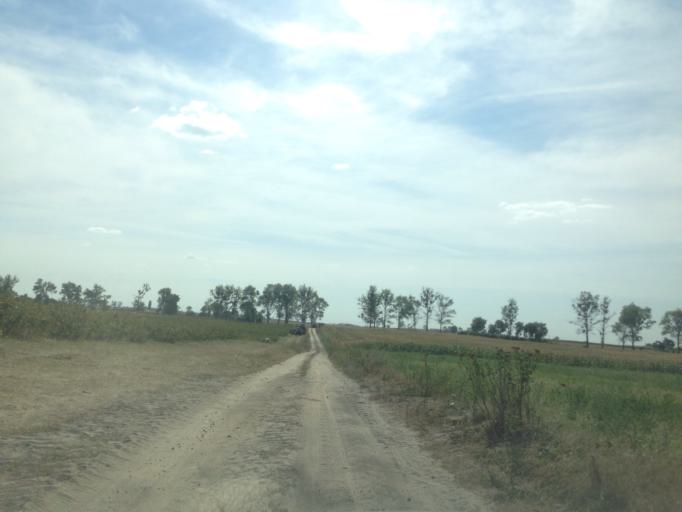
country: PL
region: Kujawsko-Pomorskie
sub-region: Powiat brodnicki
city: Gorzno
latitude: 53.2128
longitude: 19.6270
